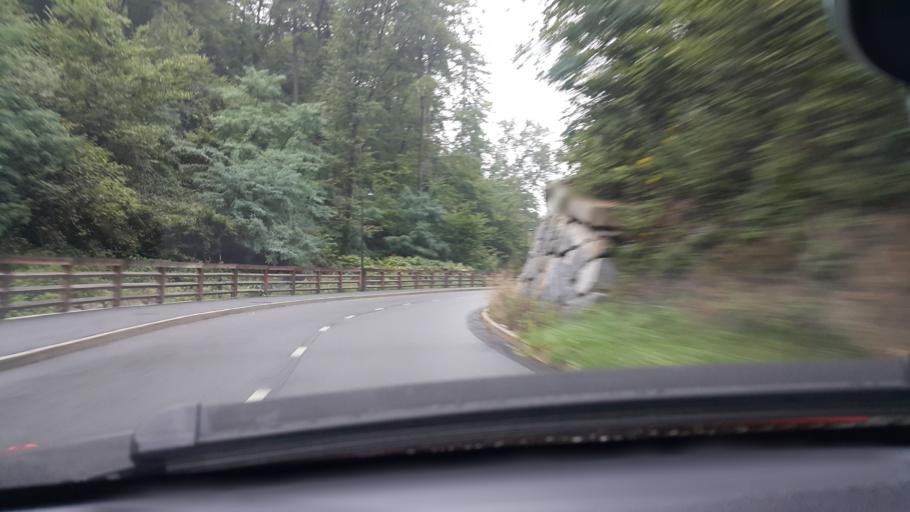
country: SI
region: Maribor
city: Maribor
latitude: 46.5694
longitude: 15.6439
